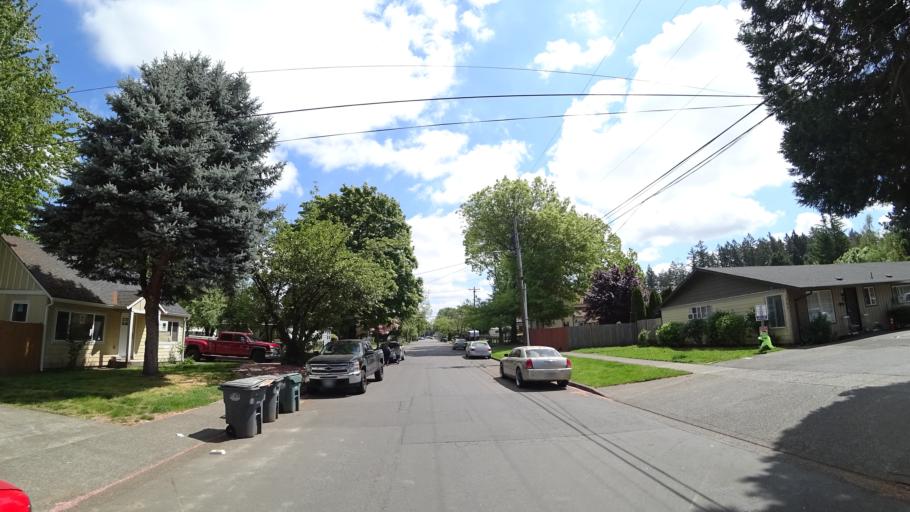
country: US
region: Oregon
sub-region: Washington County
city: Hillsboro
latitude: 45.5162
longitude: -122.9782
